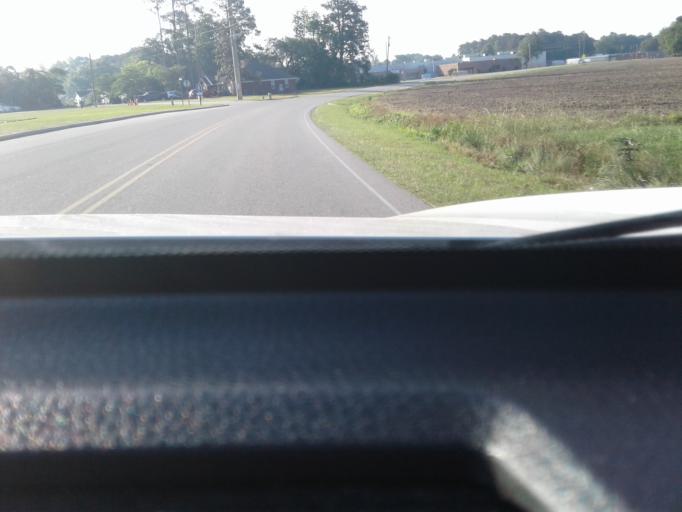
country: US
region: North Carolina
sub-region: Harnett County
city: Dunn
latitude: 35.3220
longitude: -78.6225
